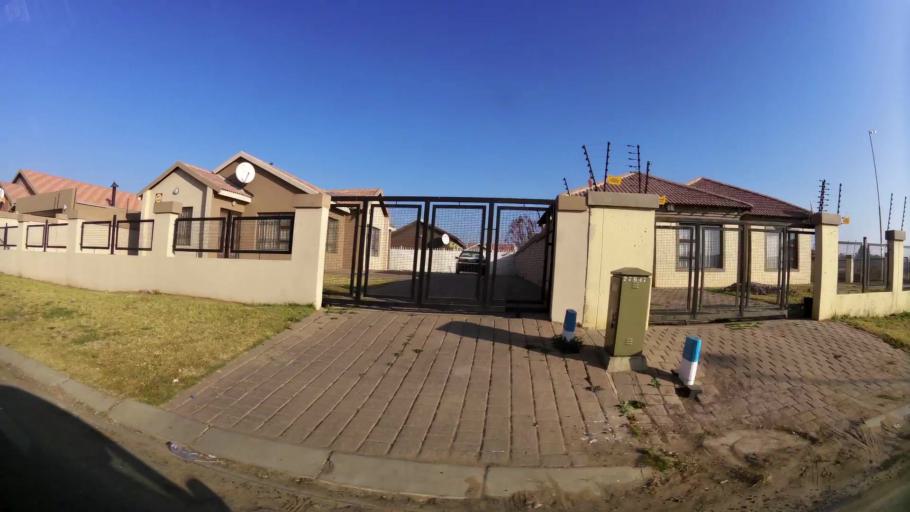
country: ZA
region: Orange Free State
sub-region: Mangaung Metropolitan Municipality
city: Bloemfontein
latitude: -29.1529
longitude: 26.2104
